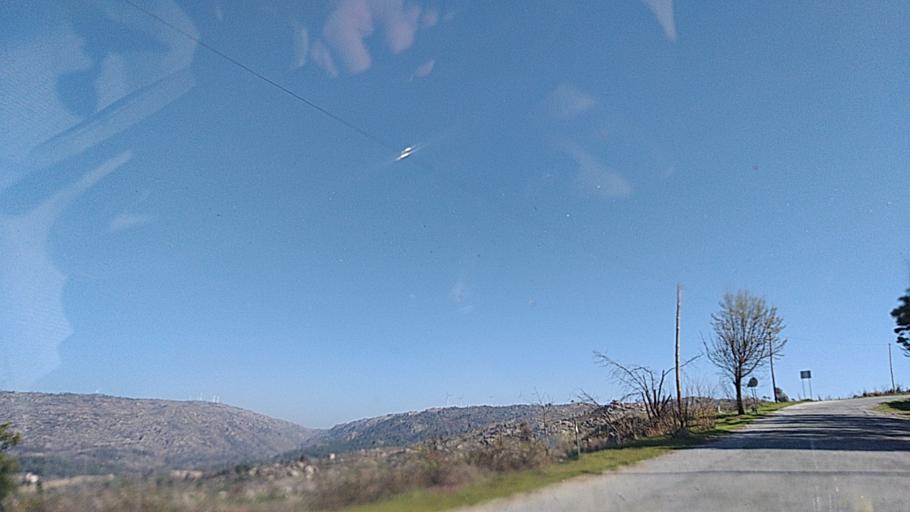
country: PT
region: Guarda
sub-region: Celorico da Beira
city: Celorico da Beira
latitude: 40.6898
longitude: -7.4401
